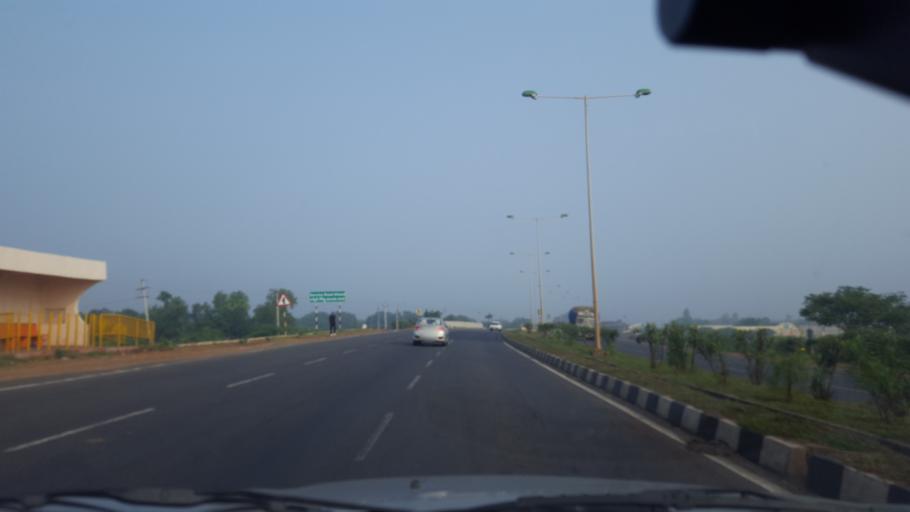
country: IN
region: Andhra Pradesh
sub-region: Prakasam
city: Ongole
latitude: 15.3859
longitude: 80.0397
